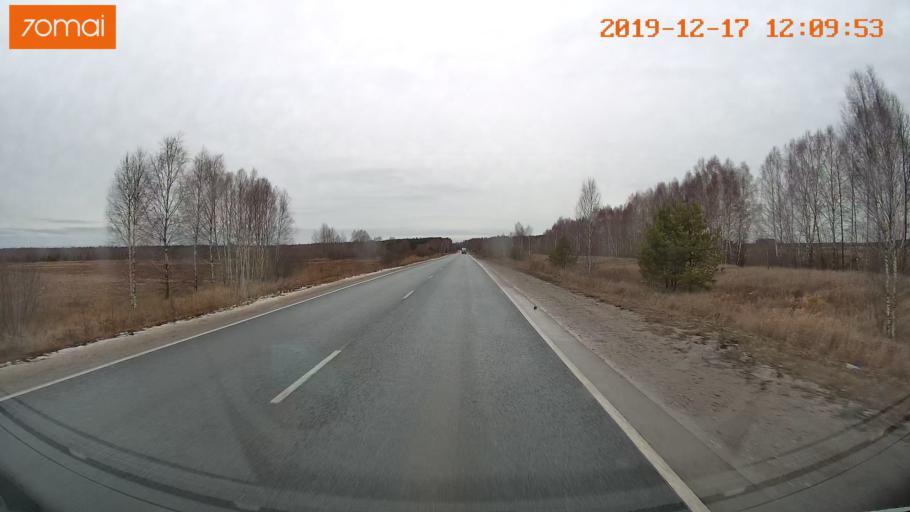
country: RU
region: Rjazan
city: Spas-Klepiki
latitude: 55.1475
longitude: 40.3068
